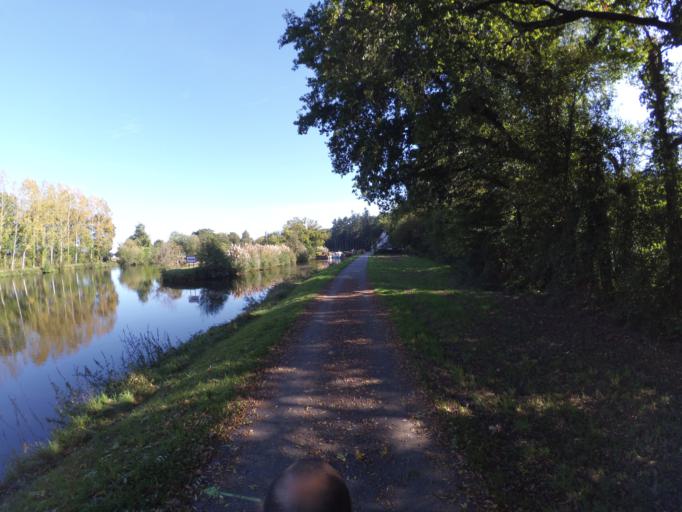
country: FR
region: Brittany
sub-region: Departement du Morbihan
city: Saint-Martin-sur-Oust
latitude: 47.7402
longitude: -2.2581
